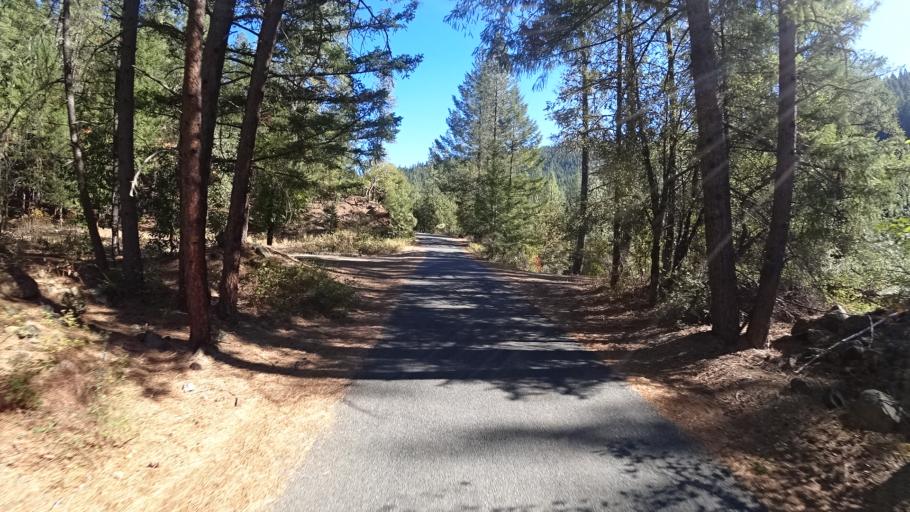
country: US
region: California
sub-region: Siskiyou County
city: Happy Camp
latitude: 41.3000
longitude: -123.1371
